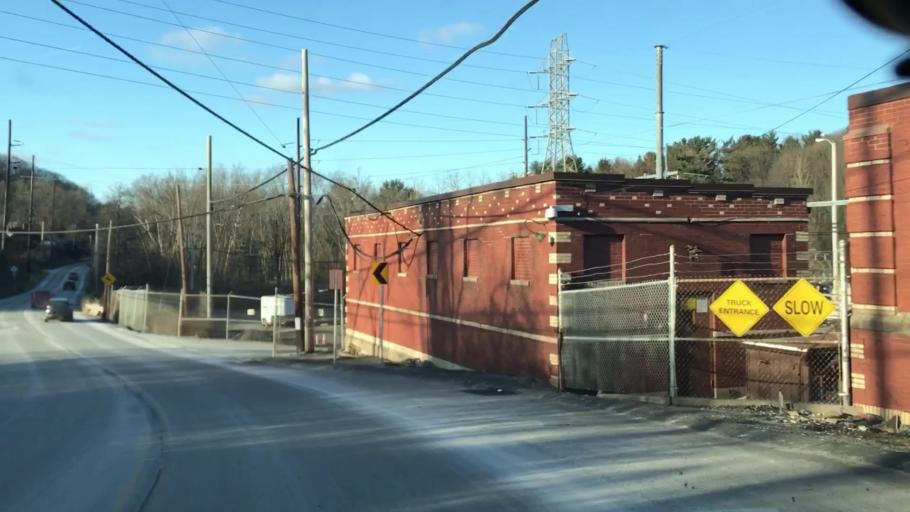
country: US
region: Pennsylvania
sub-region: Allegheny County
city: Glenshaw
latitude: 40.5402
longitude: -79.9905
